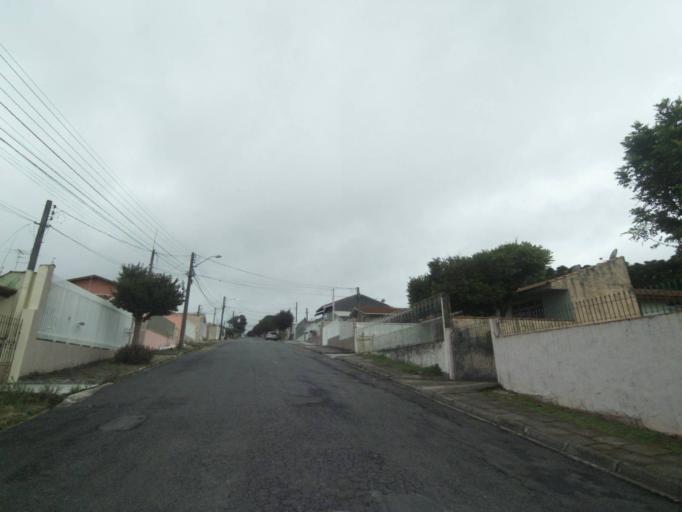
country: BR
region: Parana
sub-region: Curitiba
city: Curitiba
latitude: -25.4281
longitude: -49.3444
